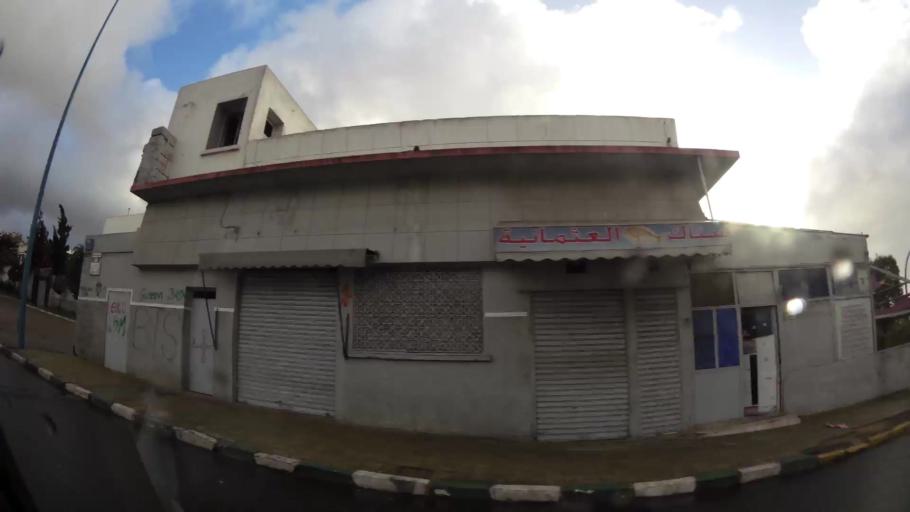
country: MA
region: Grand Casablanca
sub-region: Casablanca
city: Casablanca
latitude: 33.5597
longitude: -7.5752
